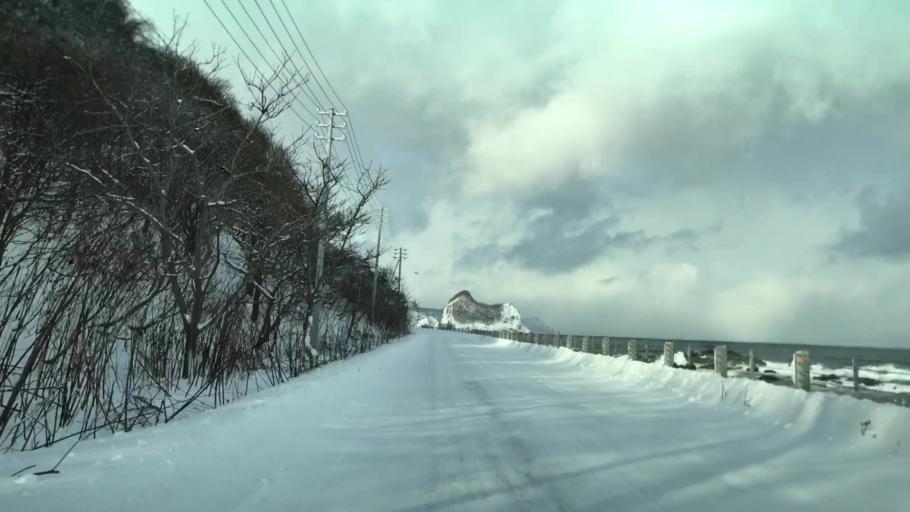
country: JP
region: Hokkaido
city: Yoichi
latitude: 43.2954
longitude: 140.6219
